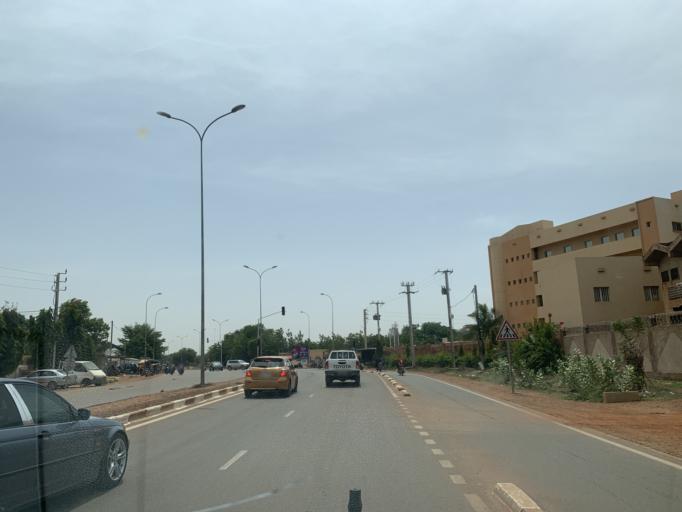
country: BF
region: Centre
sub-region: Kadiogo Province
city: Ouagadougou
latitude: 12.3374
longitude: -1.5032
